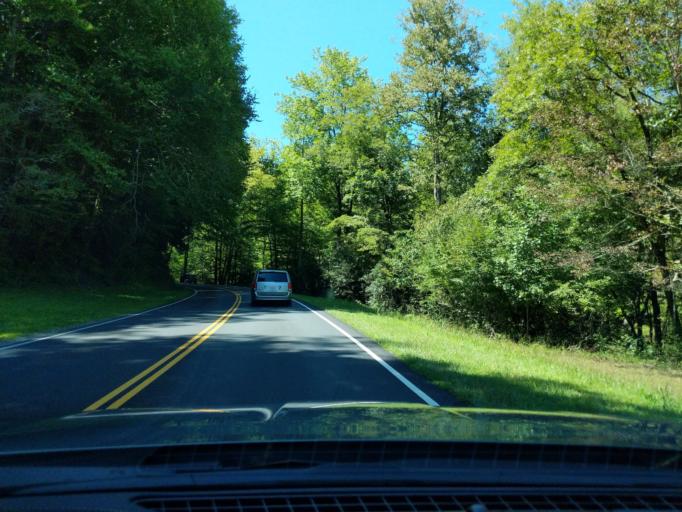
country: US
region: North Carolina
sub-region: Swain County
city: Cherokee
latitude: 35.5434
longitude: -83.3008
